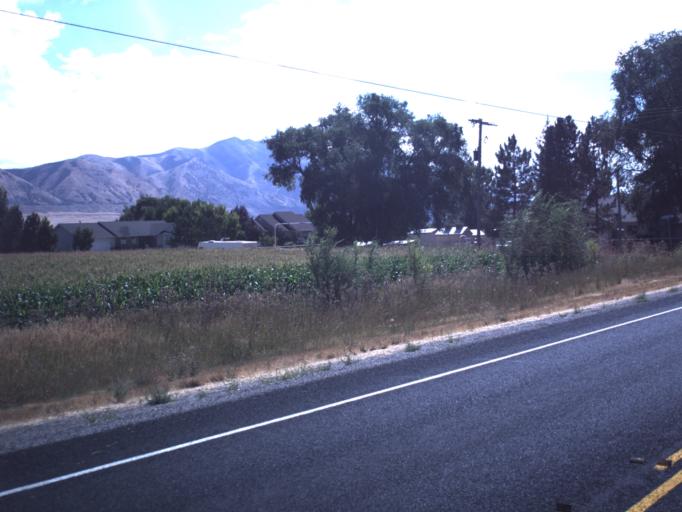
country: US
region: Utah
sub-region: Box Elder County
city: Garland
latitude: 41.7711
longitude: -112.1490
